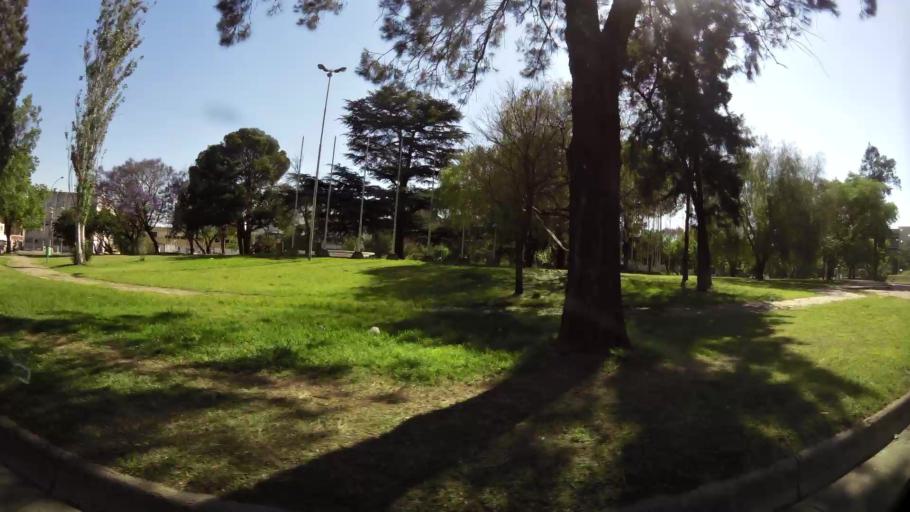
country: AR
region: Cordoba
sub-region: Departamento de Capital
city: Cordoba
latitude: -31.4334
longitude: -64.1946
